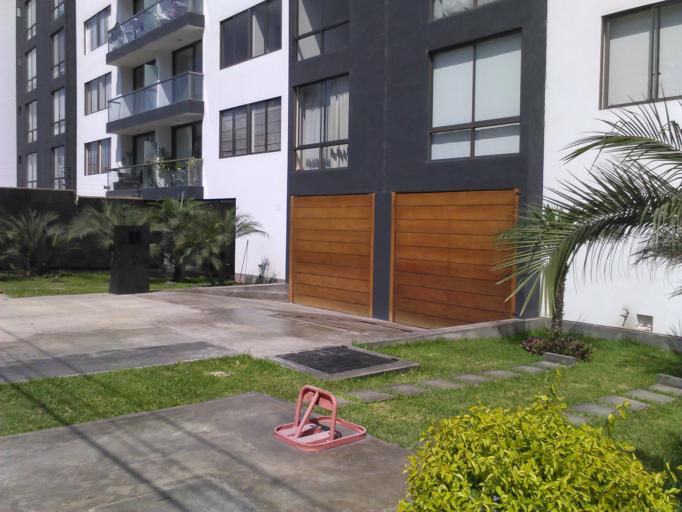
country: PE
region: Lima
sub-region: Lima
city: San Isidro
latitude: -12.0926
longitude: -77.0430
